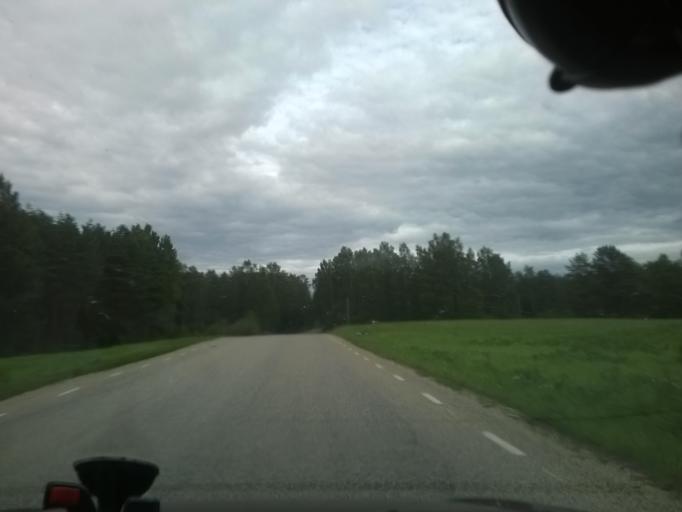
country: EE
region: Vorumaa
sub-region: Voru linn
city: Voru
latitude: 57.7694
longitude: 27.0199
